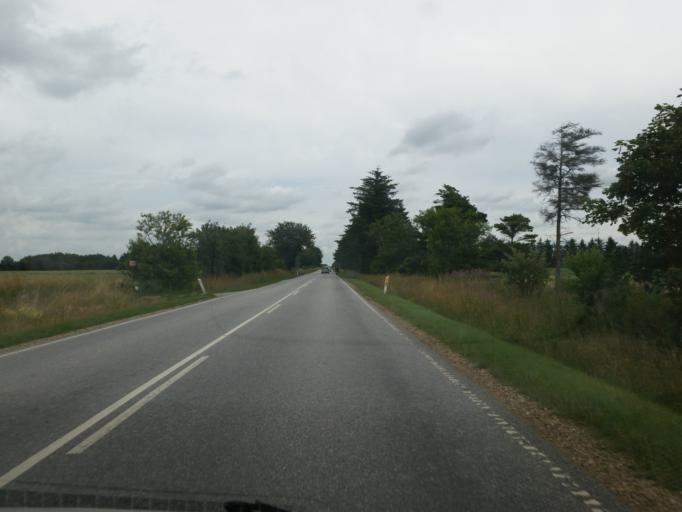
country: DK
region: South Denmark
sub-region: Esbjerg Kommune
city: Ribe
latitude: 55.3781
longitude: 8.8273
